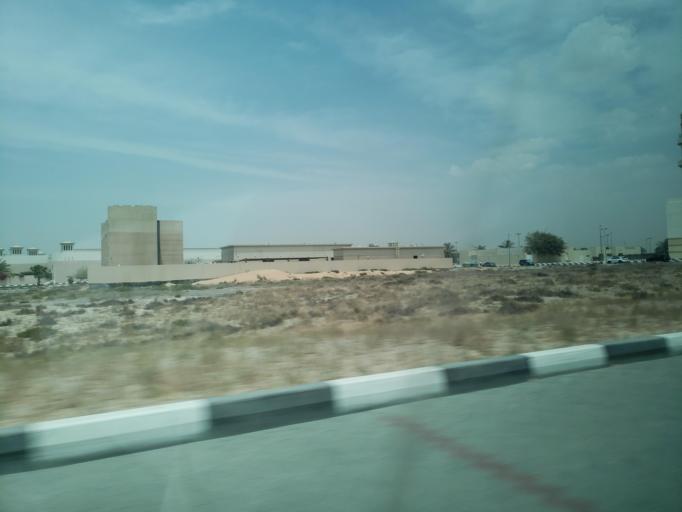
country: AE
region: Ash Shariqah
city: Sharjah
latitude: 25.3152
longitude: 55.5128
